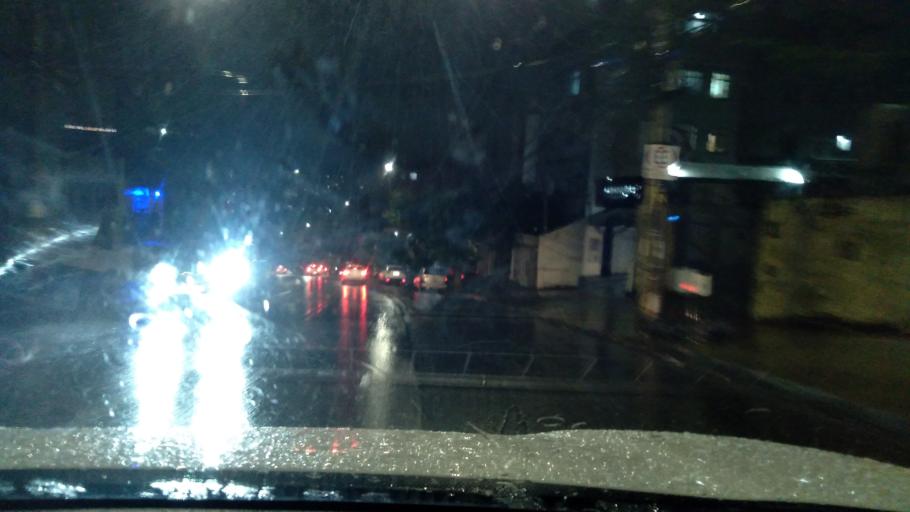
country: BR
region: Minas Gerais
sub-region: Belo Horizonte
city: Belo Horizonte
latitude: -19.8748
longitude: -43.9367
